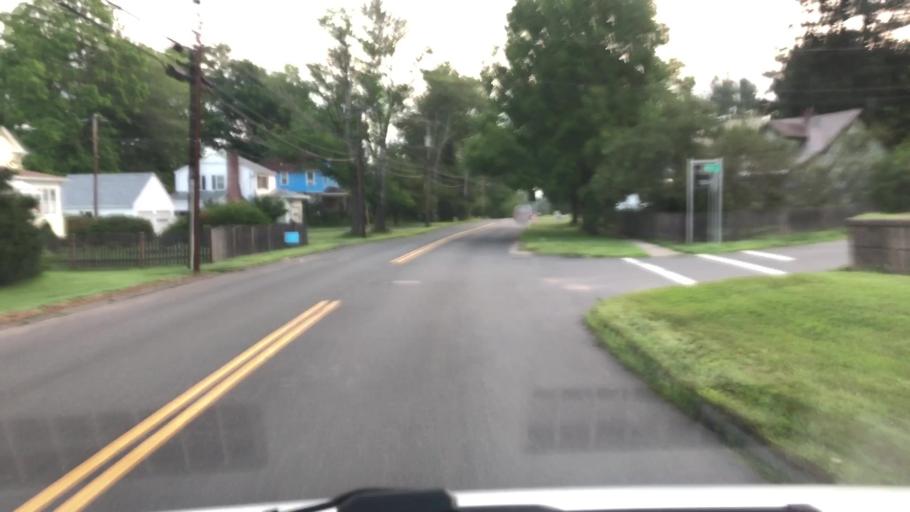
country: US
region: Massachusetts
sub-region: Hampshire County
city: Easthampton
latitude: 42.2588
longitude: -72.6789
